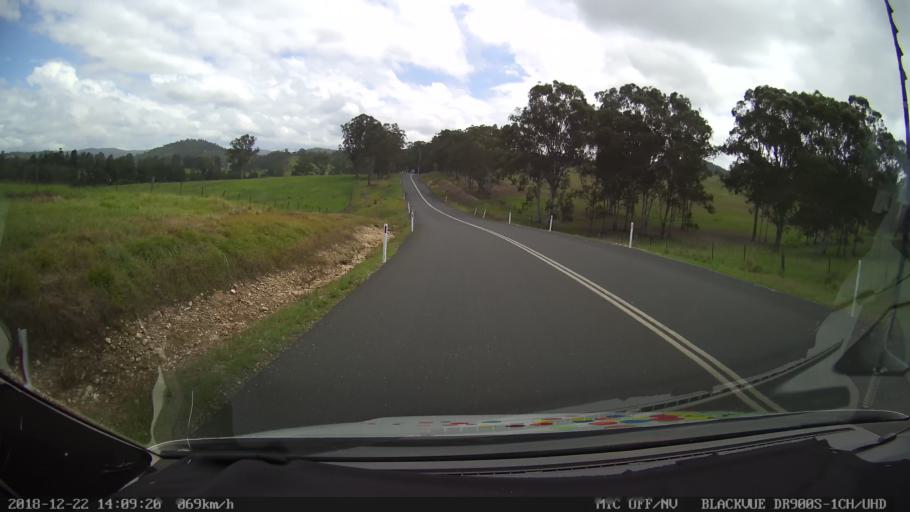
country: AU
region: New South Wales
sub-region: Clarence Valley
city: Coutts Crossing
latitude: -29.9855
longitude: 152.7181
